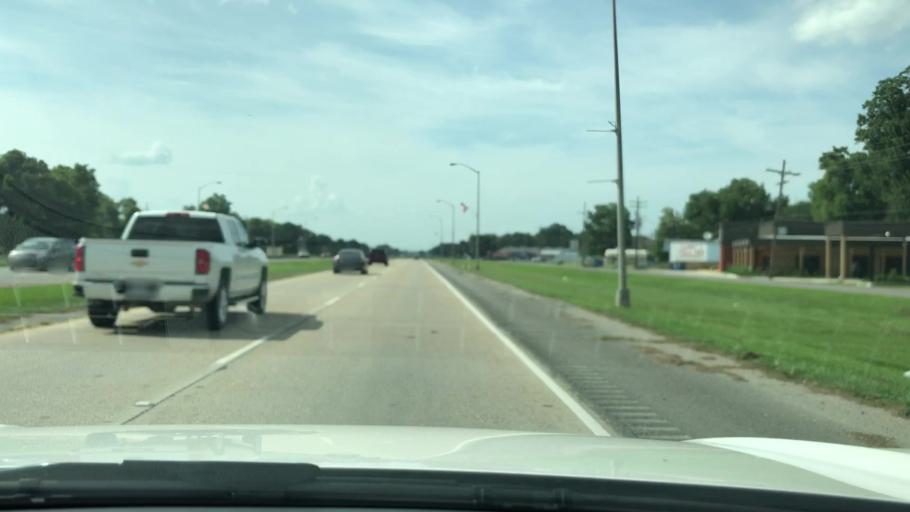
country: US
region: Louisiana
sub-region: Iberville Parish
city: Plaquemine
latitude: 30.3044
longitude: -91.2444
